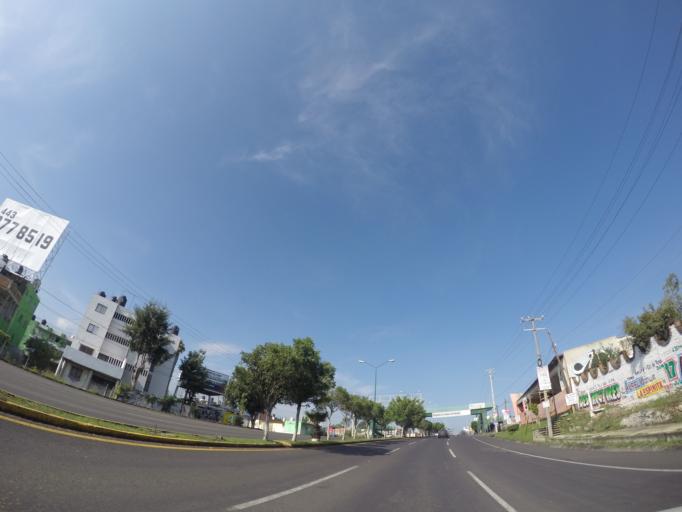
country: MX
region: Michoacan
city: Morelia
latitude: 19.6754
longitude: -101.2031
